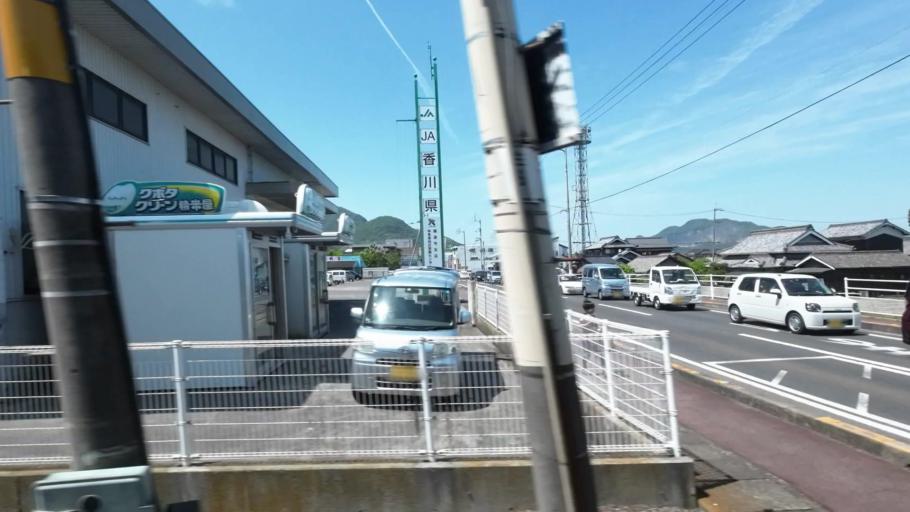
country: JP
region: Kagawa
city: Marugame
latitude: 34.2355
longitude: 133.7861
